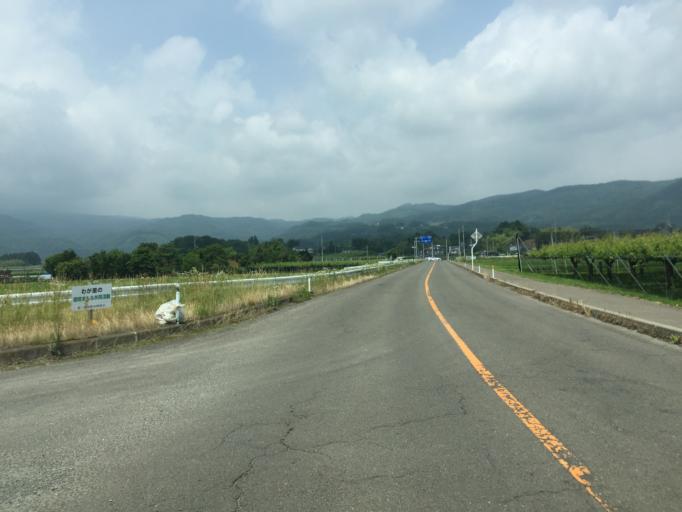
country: JP
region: Fukushima
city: Fukushima-shi
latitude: 37.7664
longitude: 140.3849
